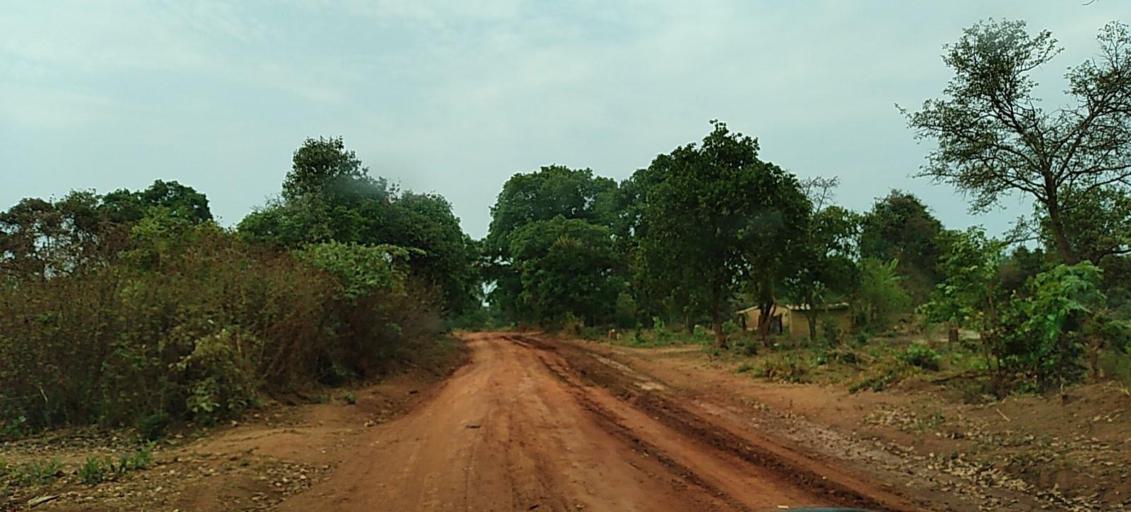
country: ZM
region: North-Western
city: Solwezi
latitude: -12.2474
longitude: 26.5128
